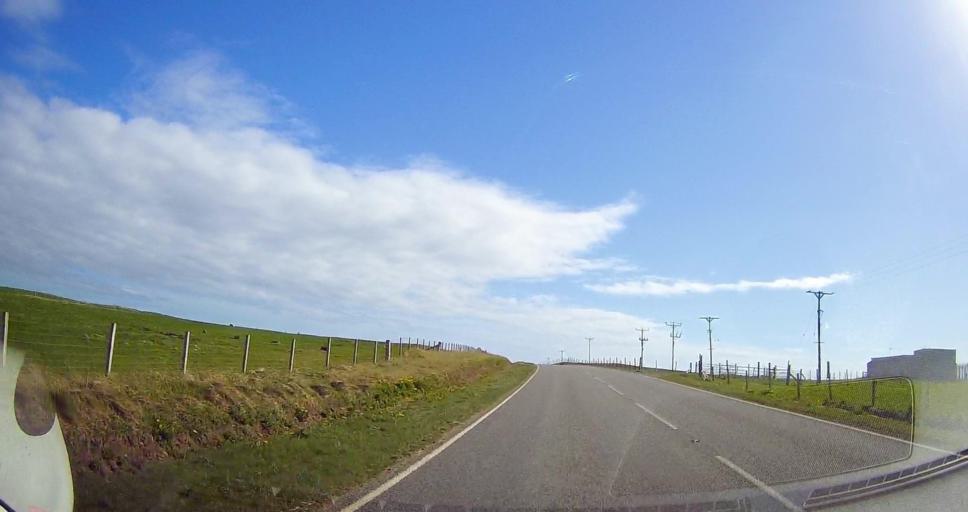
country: GB
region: Scotland
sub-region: Shetland Islands
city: Sandwick
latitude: 59.8993
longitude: -1.3035
